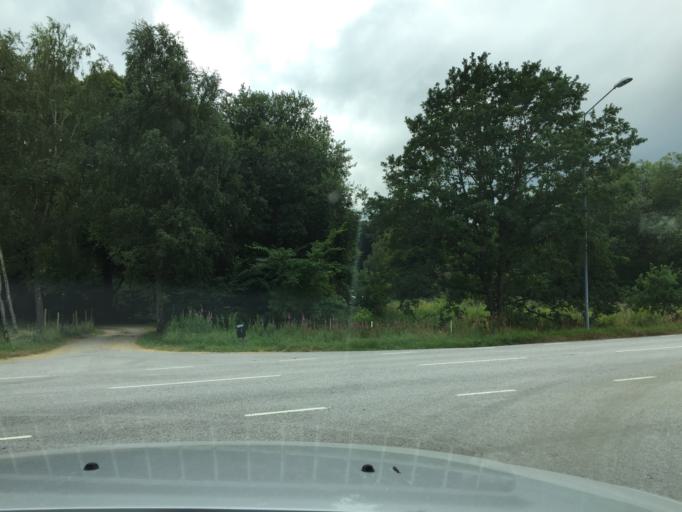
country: SE
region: Skane
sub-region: Hassleholms Kommun
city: Sosdala
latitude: 56.0080
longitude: 13.6455
